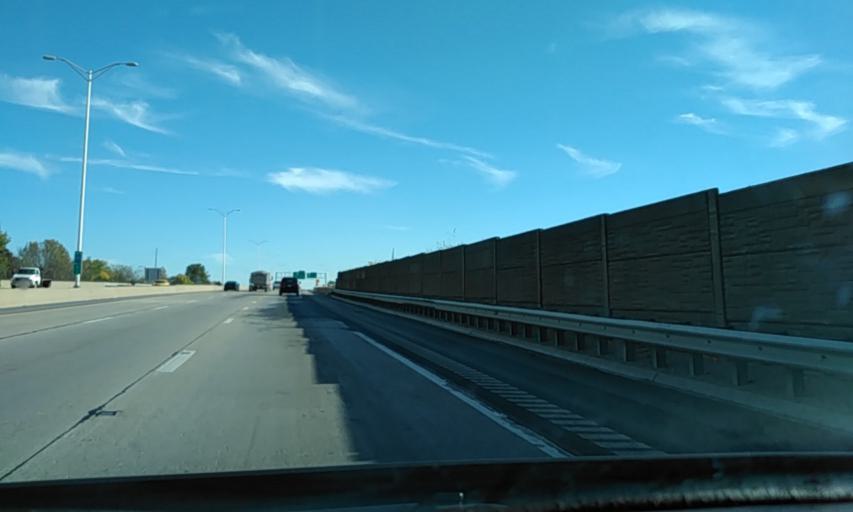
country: US
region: Illinois
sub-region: Saint Clair County
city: Centreville
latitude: 38.5767
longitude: -90.1155
